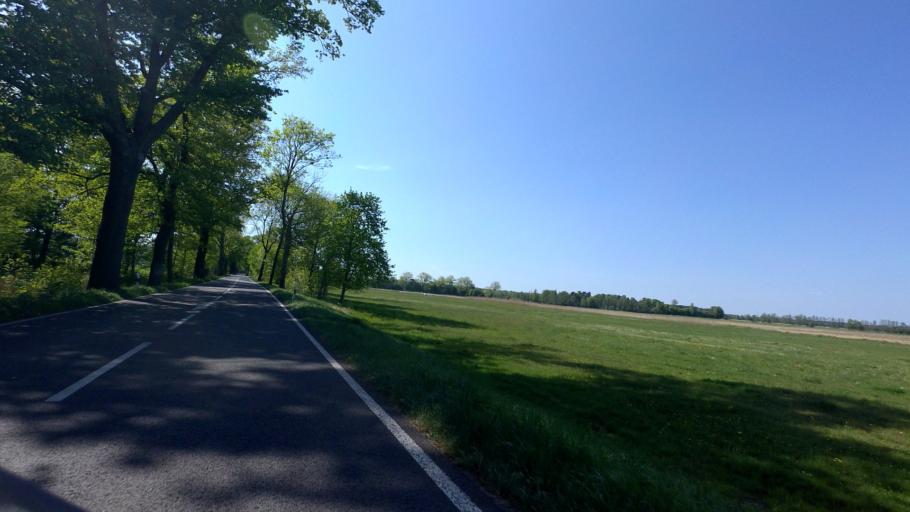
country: DE
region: Brandenburg
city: Schlepzig
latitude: 52.0621
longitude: 13.9352
